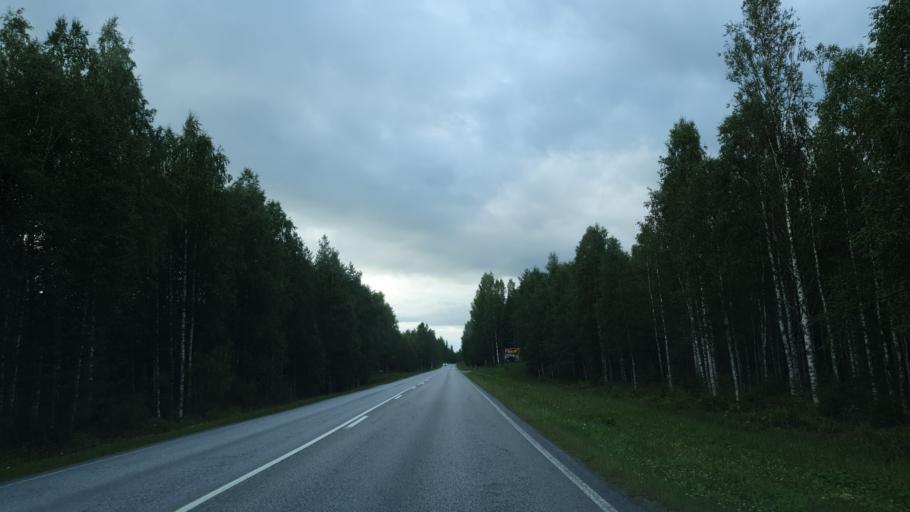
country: FI
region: North Karelia
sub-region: Joensuu
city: Eno
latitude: 63.0501
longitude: 30.1264
